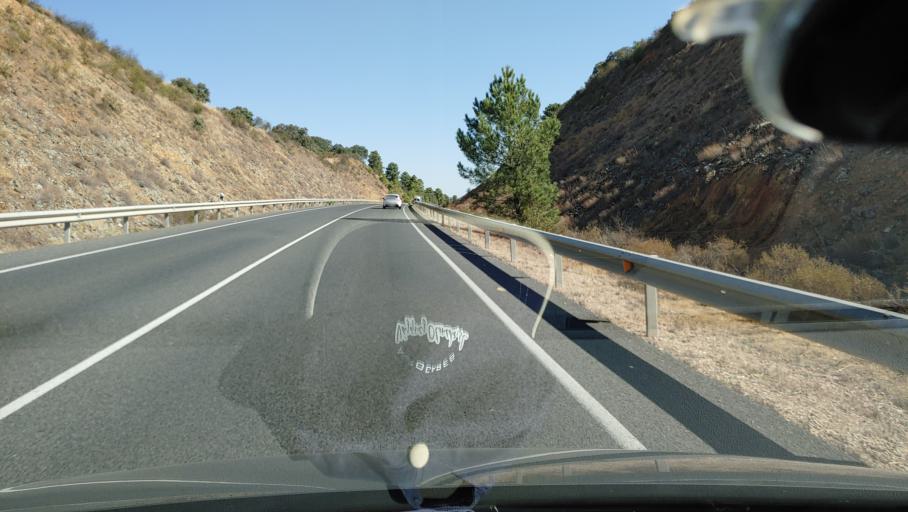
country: ES
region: Andalusia
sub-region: Province of Cordoba
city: Obejo
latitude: 38.0268
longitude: -4.8102
